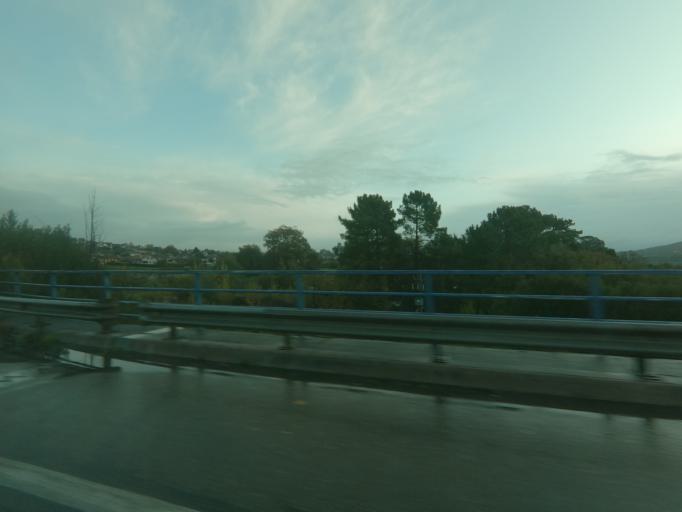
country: PT
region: Viana do Castelo
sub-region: Valenca
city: Valenca
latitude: 42.0349
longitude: -8.6551
